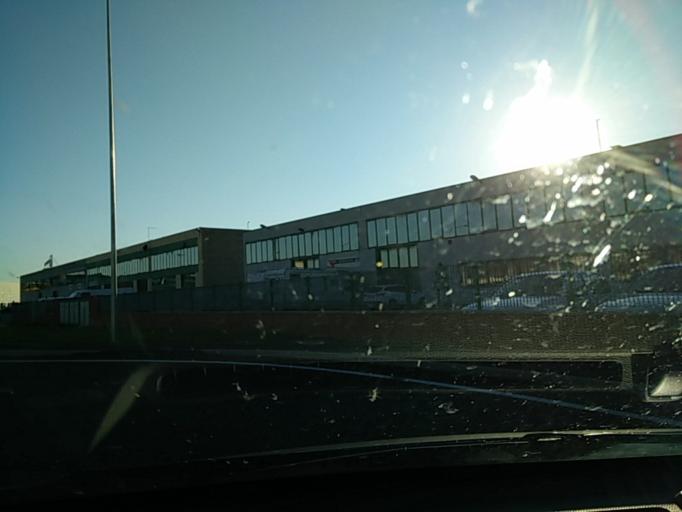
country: IT
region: Veneto
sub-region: Provincia di Venezia
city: Quarto d'Altino
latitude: 45.5801
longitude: 12.3503
